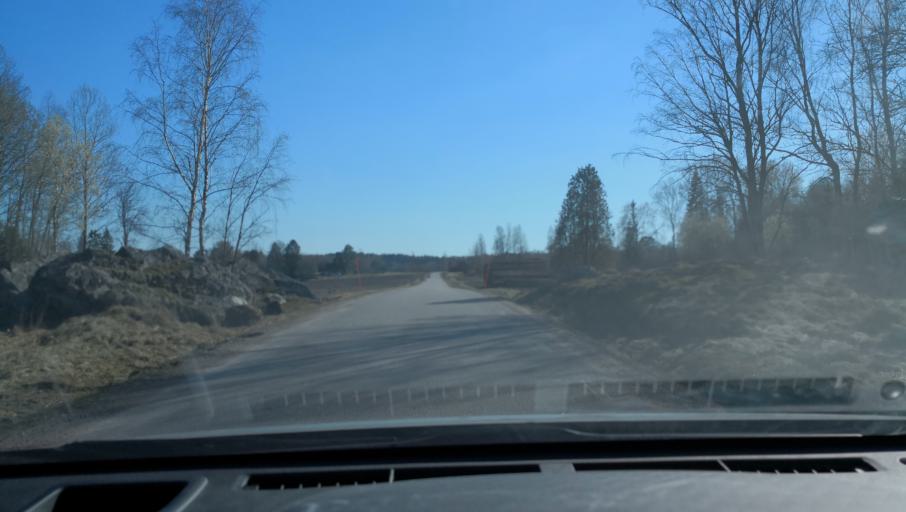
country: SE
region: Vaestmanland
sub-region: Sala Kommun
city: Sala
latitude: 60.0819
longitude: 16.4972
